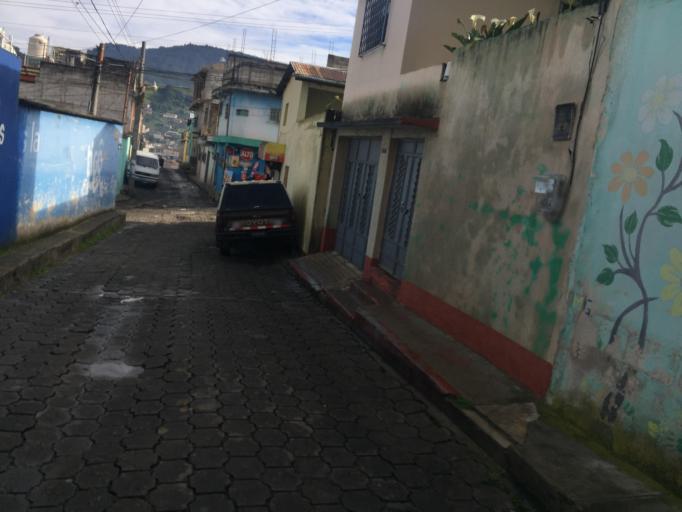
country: GT
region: Totonicapan
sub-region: Municipio de Totonicapan
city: Totonicapan
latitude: 14.9120
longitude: -91.3569
